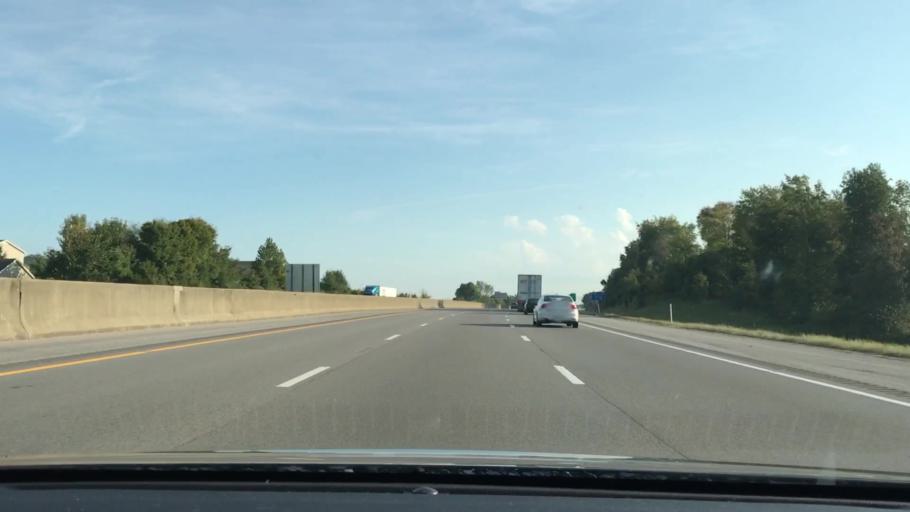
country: US
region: Kentucky
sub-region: Warren County
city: Bowling Green
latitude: 36.9927
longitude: -86.3826
